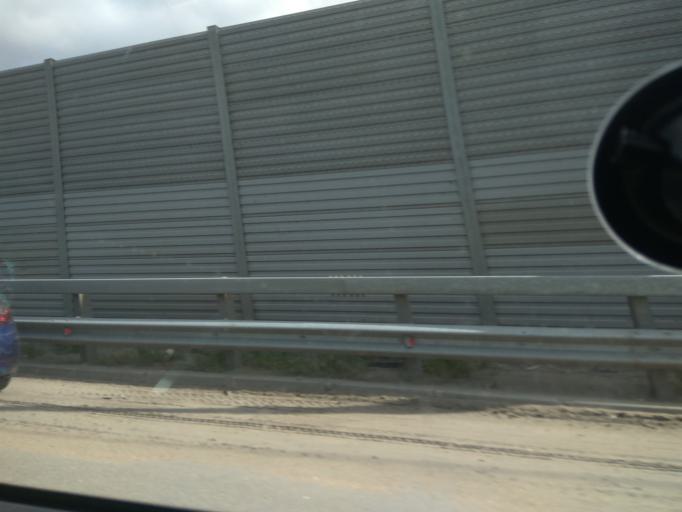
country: RU
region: Moskovskaya
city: Ostrovtsy
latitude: 55.5637
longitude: 38.0486
